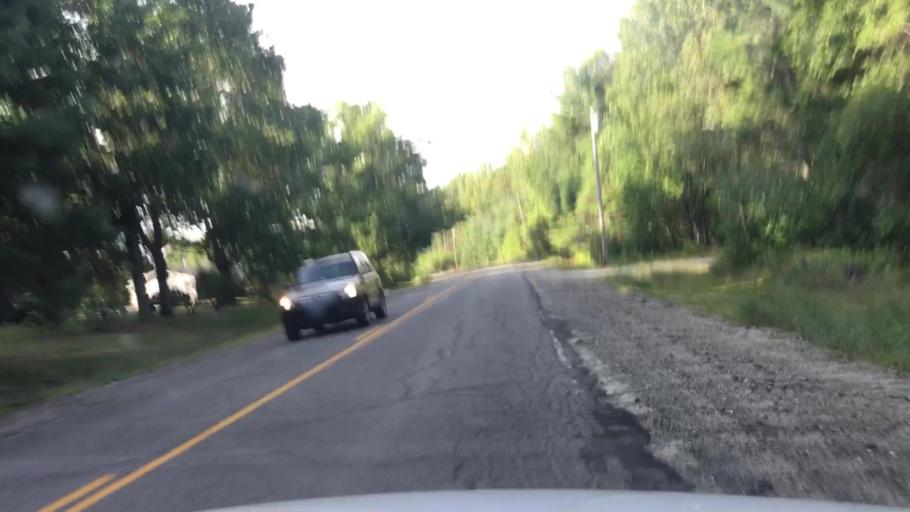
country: US
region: Maine
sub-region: Penobscot County
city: Enfield
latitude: 45.2344
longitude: -68.5439
